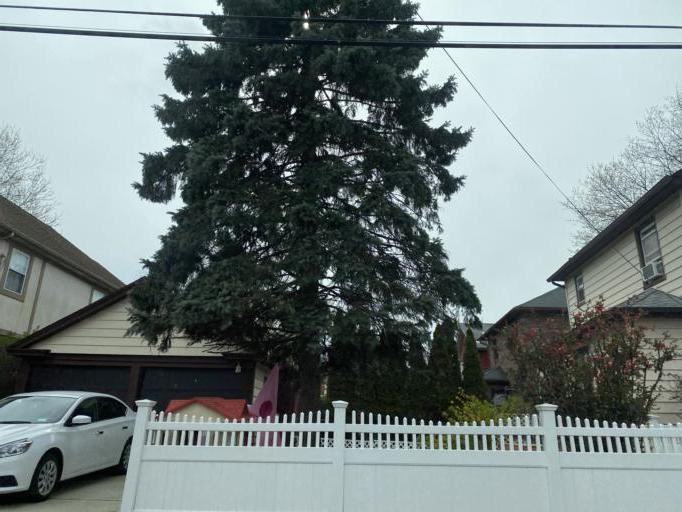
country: US
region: New York
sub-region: Nassau County
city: Bellerose
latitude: 40.7203
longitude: -73.7187
